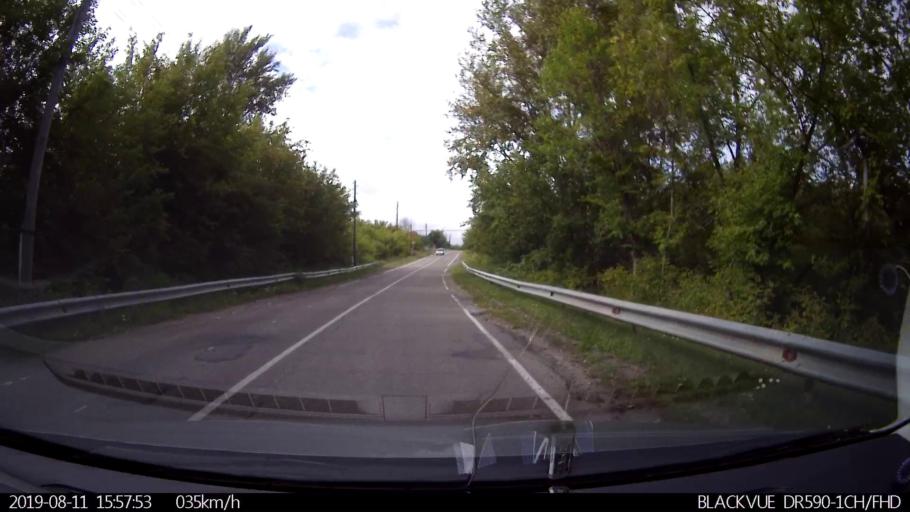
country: RU
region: Ulyanovsk
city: Ignatovka
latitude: 53.9530
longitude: 47.6508
